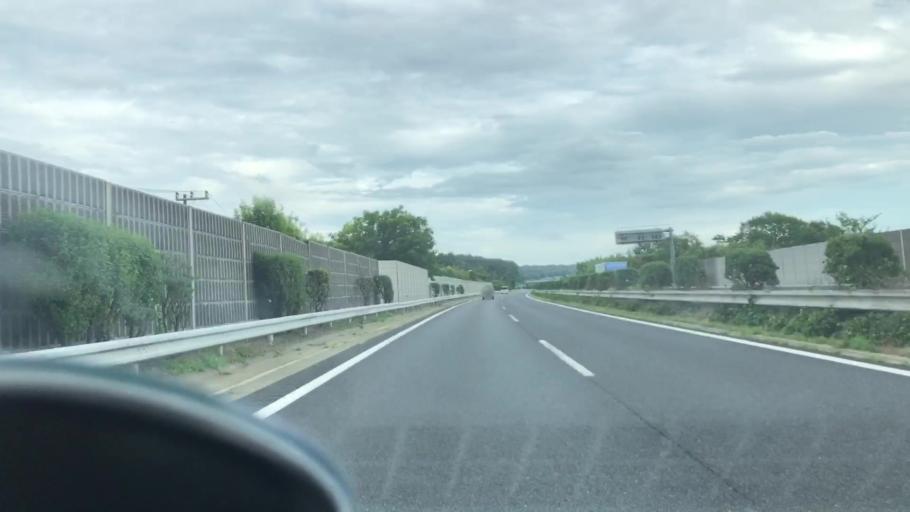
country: JP
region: Hyogo
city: Yashiro
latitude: 34.9264
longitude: 134.9861
